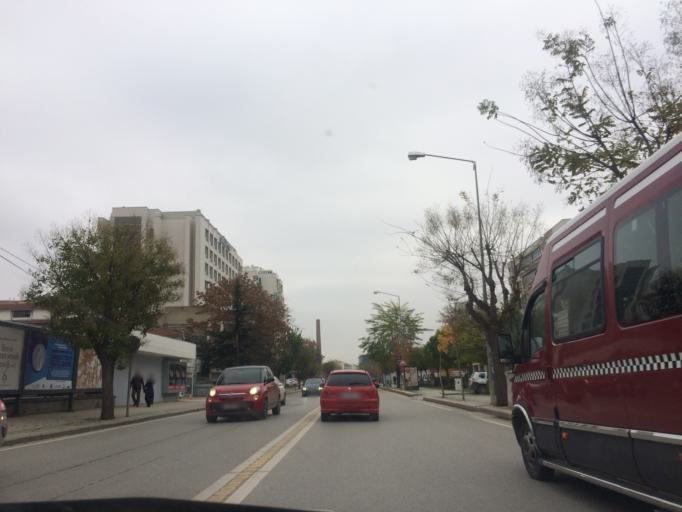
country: TR
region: Eskisehir
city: Eskisehir
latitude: 39.7836
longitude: 30.5046
